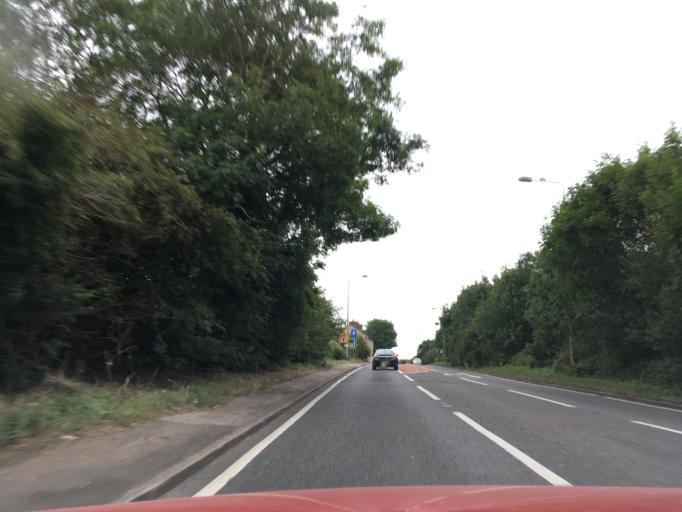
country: GB
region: England
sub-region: Central Bedfordshire
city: Hockliffe
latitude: 51.9253
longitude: -0.5775
